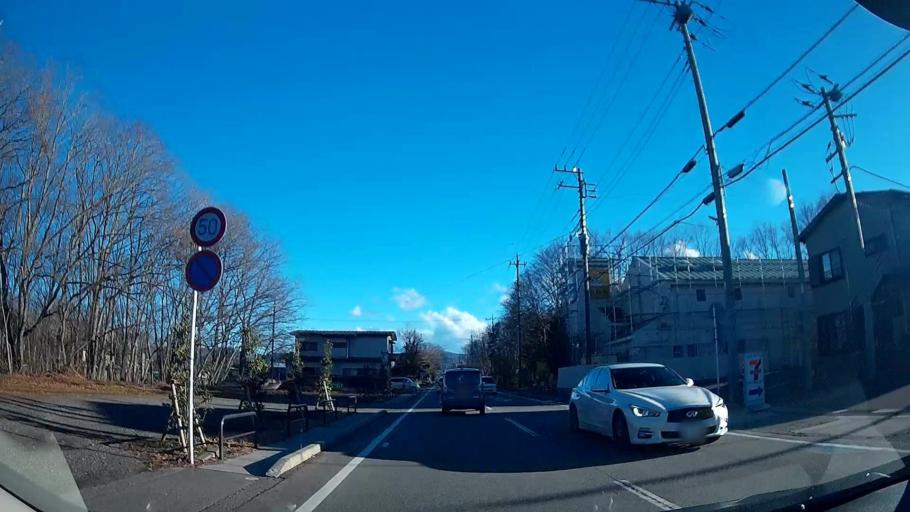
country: JP
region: Shizuoka
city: Gotemba
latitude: 35.4319
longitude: 138.8435
